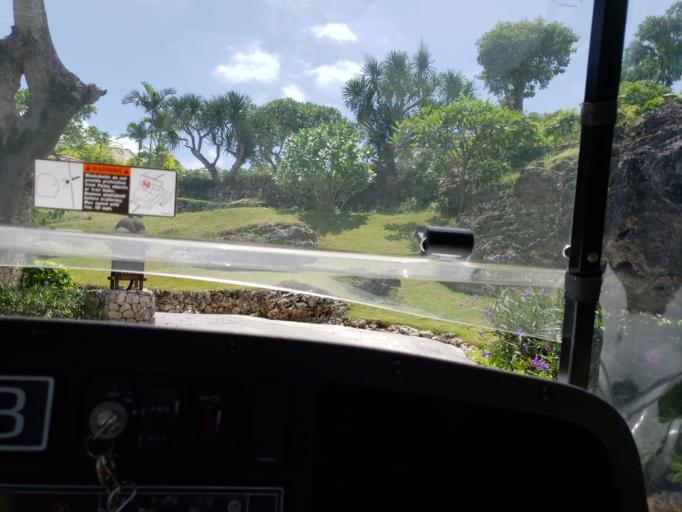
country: ID
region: Bali
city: Jimbaran
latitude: -8.7824
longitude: 115.1591
